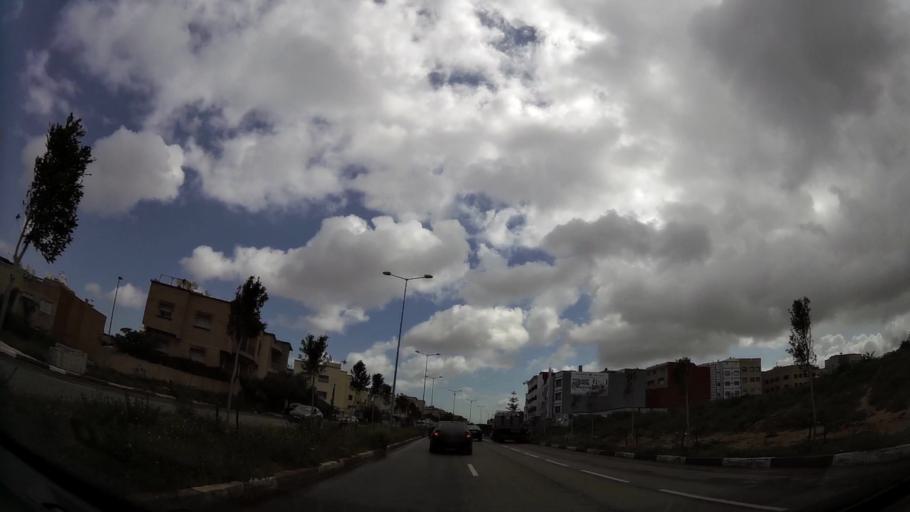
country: MA
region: Grand Casablanca
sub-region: Casablanca
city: Casablanca
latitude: 33.5310
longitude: -7.5895
